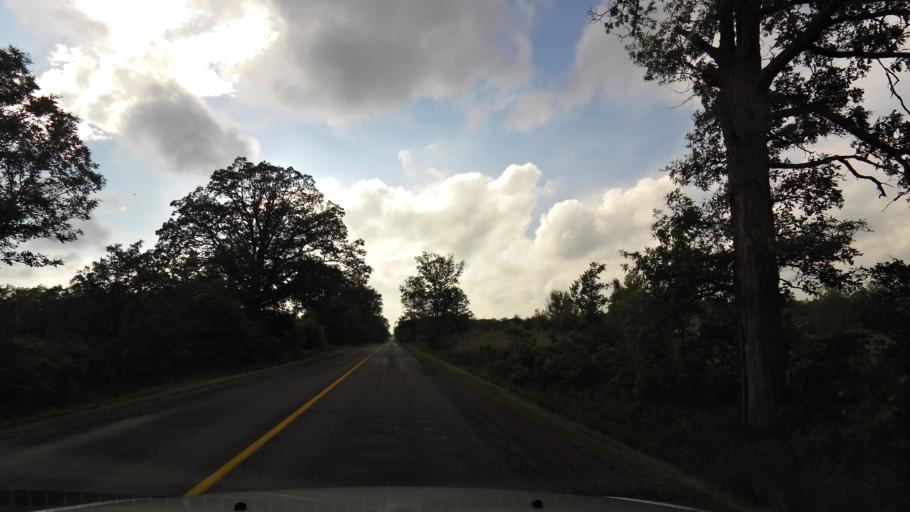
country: CA
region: Ontario
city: Ancaster
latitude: 43.0123
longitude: -80.0768
